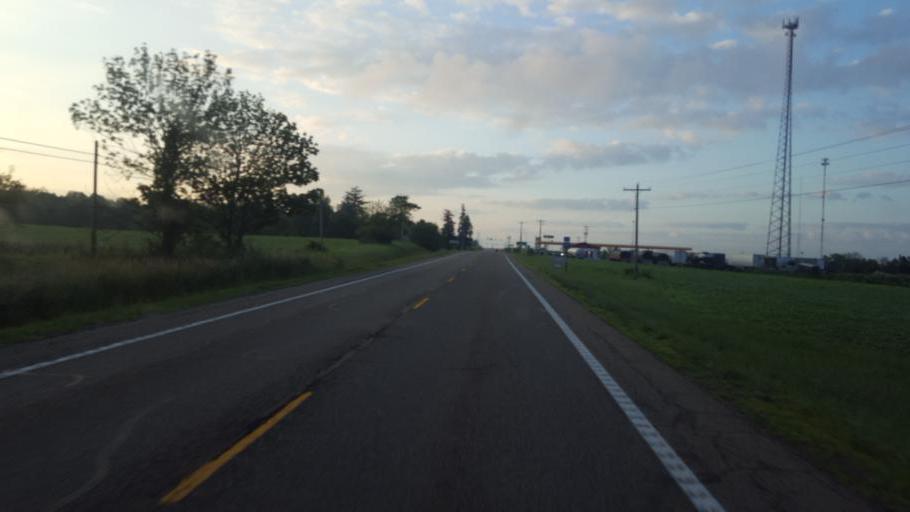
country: US
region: Ohio
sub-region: Morrow County
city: Mount Gilead
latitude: 40.4995
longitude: -82.7230
